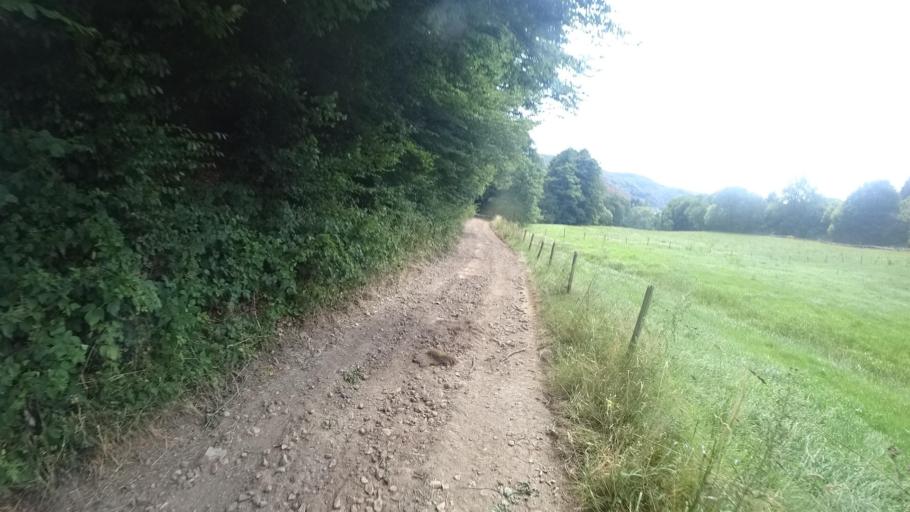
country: DE
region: Rheinland-Pfalz
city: Heckenbach
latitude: 50.4868
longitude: 7.0626
